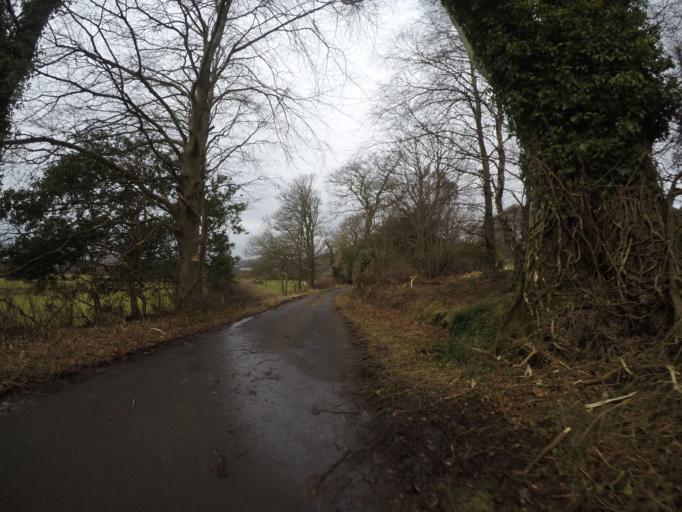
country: GB
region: Scotland
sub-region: North Ayrshire
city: Fairlie
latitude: 55.7627
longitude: -4.8475
